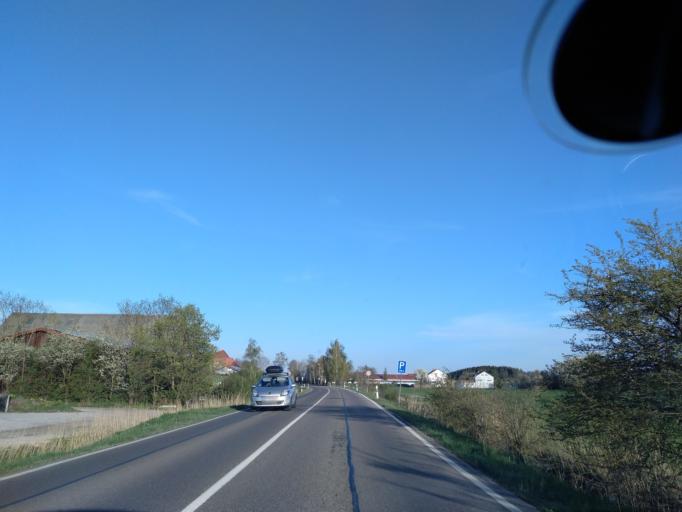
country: DE
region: Baden-Wuerttemberg
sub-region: Regierungsbezirk Stuttgart
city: Kirchberg an der Jagst
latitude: 49.1419
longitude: 9.9936
